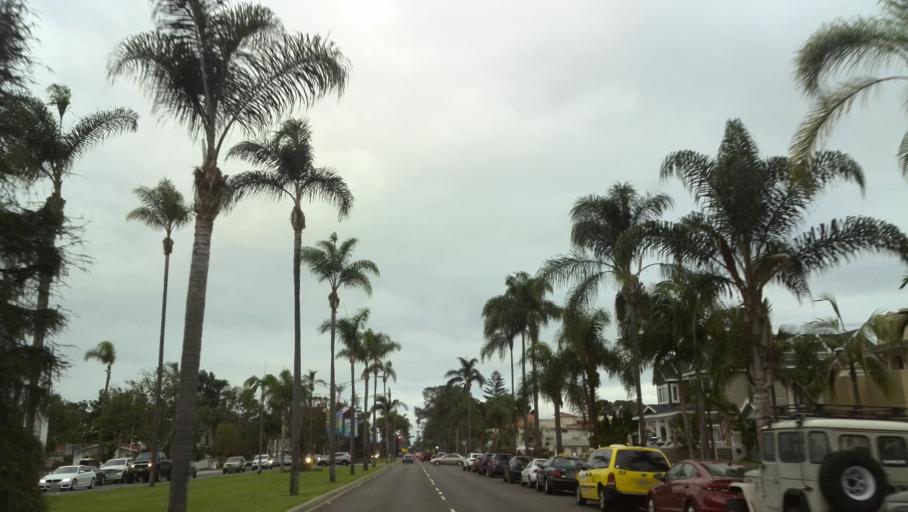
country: US
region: California
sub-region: San Diego County
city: Coronado
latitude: 32.6940
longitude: -117.1753
